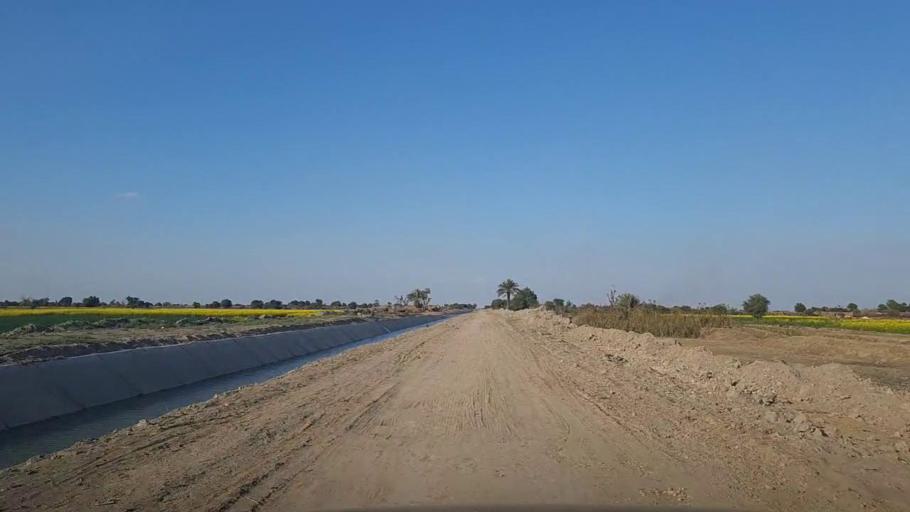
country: PK
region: Sindh
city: Jhol
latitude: 25.9020
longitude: 69.0393
